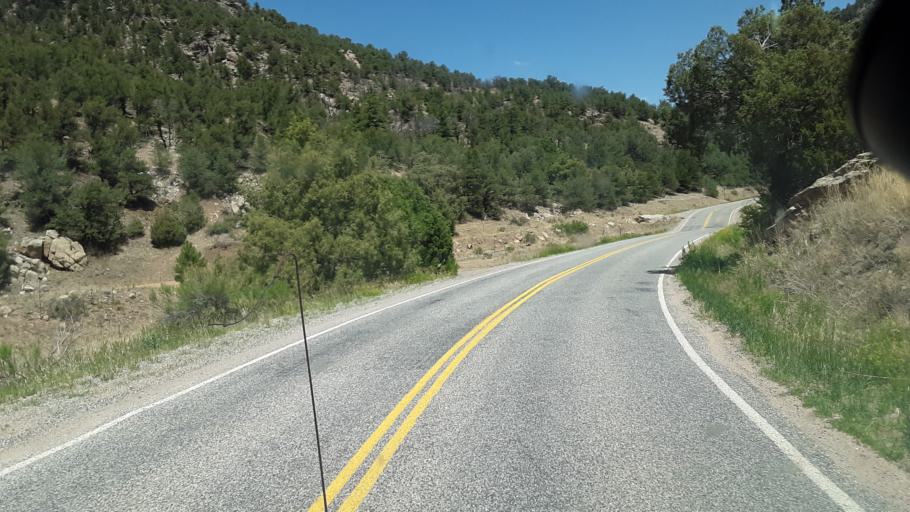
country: US
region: Colorado
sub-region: Fremont County
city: Canon City
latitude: 38.3885
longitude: -105.4552
